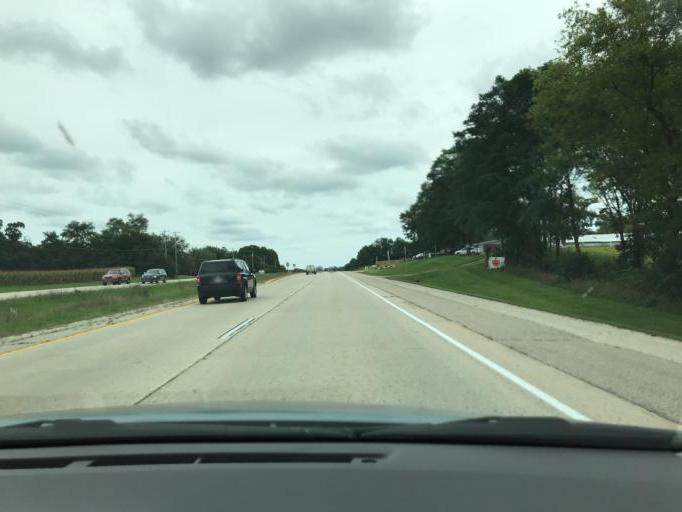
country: US
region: Wisconsin
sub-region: Kenosha County
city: Paddock Lake
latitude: 42.5680
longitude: -88.0793
